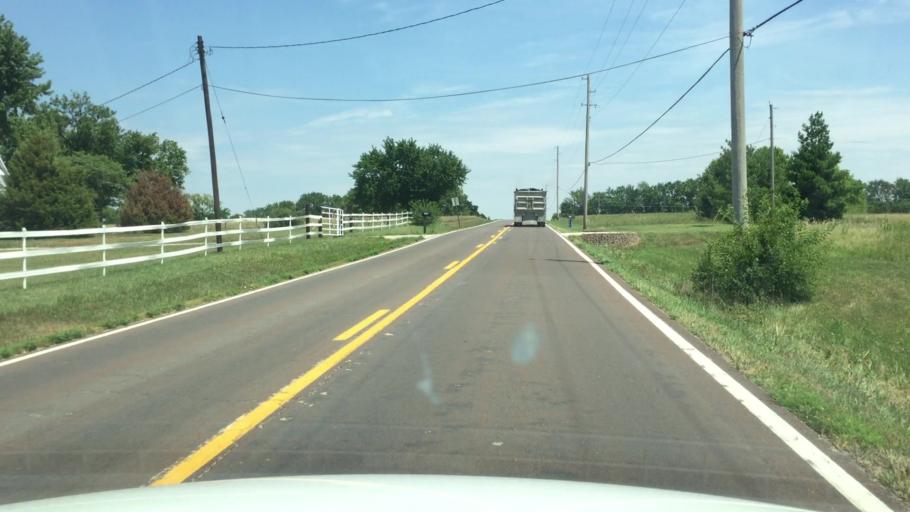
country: US
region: Kansas
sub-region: Shawnee County
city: Topeka
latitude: 38.9861
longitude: -95.5506
